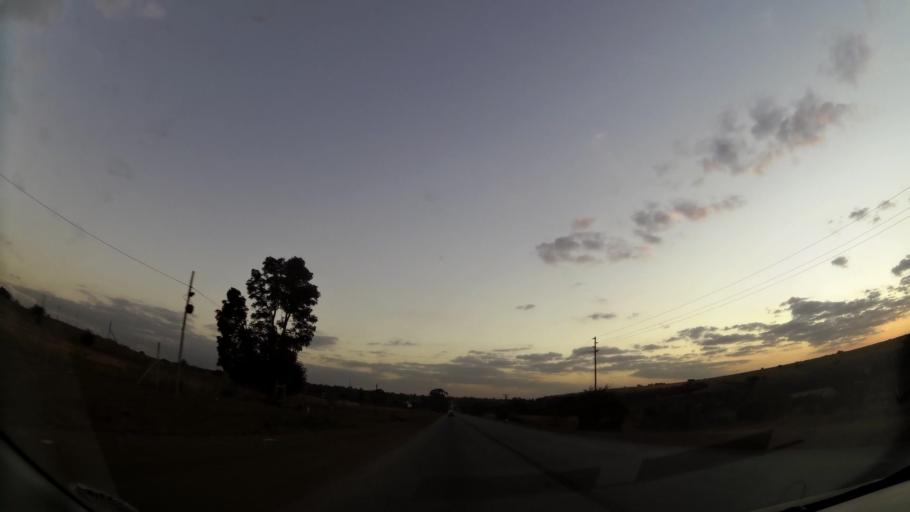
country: ZA
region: Gauteng
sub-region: West Rand District Municipality
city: Krugersdorp
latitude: -26.0608
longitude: 27.7006
